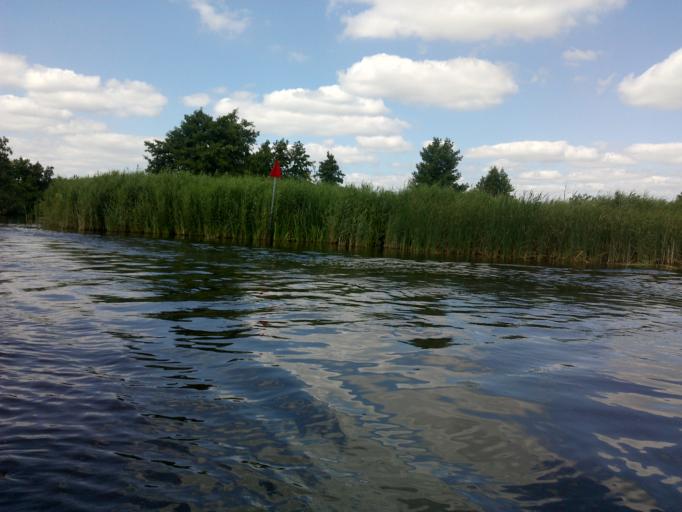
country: NL
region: Overijssel
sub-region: Gemeente Steenwijkerland
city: Giethoorn
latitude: 52.7046
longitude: 6.0788
